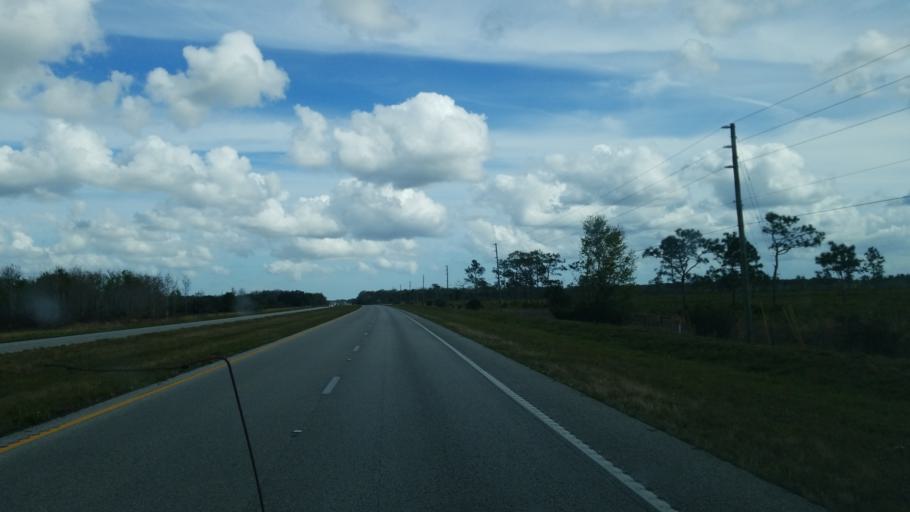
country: US
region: Florida
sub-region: Osceola County
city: Saint Cloud
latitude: 28.1323
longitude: -81.0149
